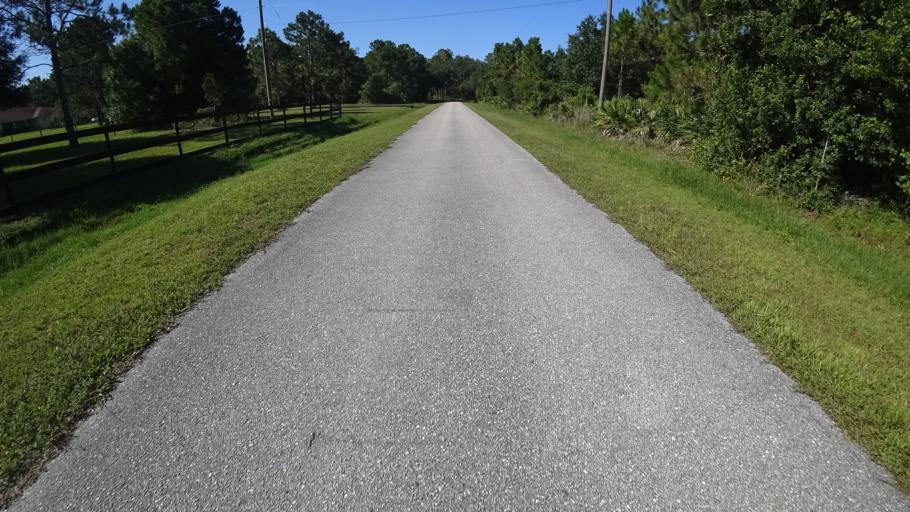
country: US
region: Florida
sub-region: Sarasota County
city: The Meadows
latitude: 27.4140
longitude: -82.3079
